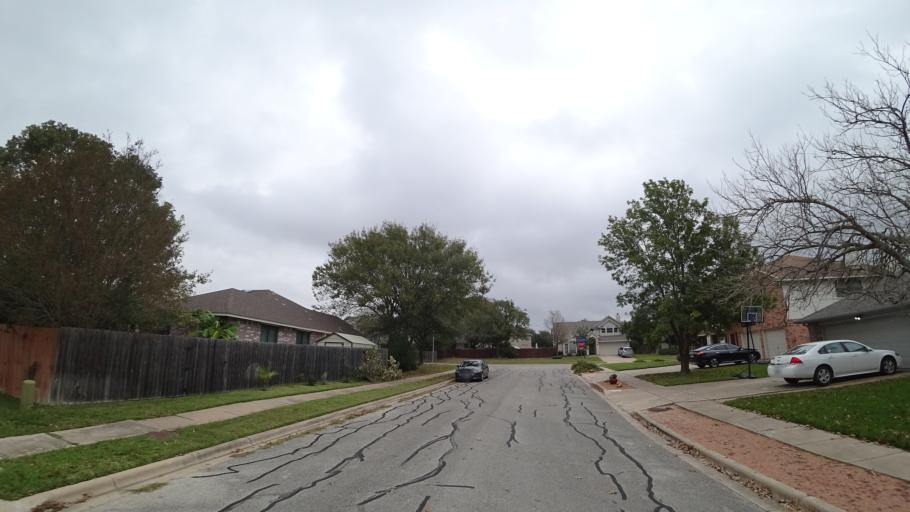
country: US
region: Texas
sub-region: Travis County
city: Pflugerville
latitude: 30.4501
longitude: -97.6122
